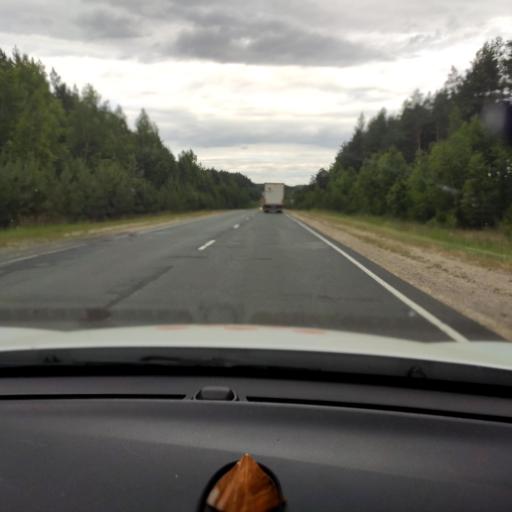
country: RU
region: Mariy-El
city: Volzhsk
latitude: 55.9030
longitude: 48.3822
